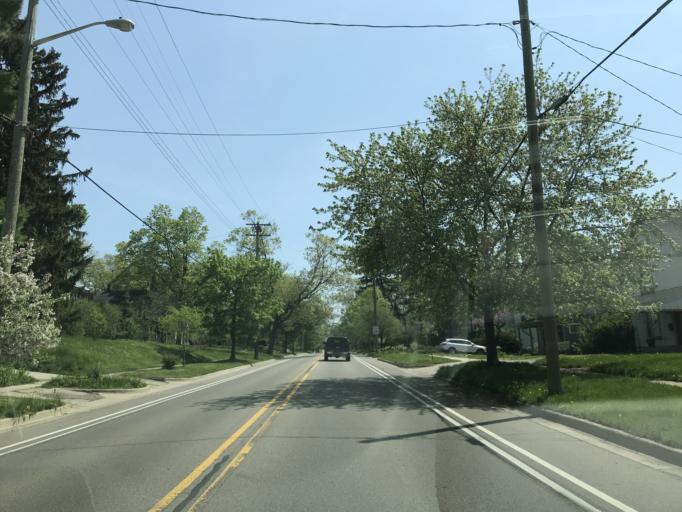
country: US
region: Michigan
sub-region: Washtenaw County
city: Ann Arbor
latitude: 42.2722
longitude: -83.7584
